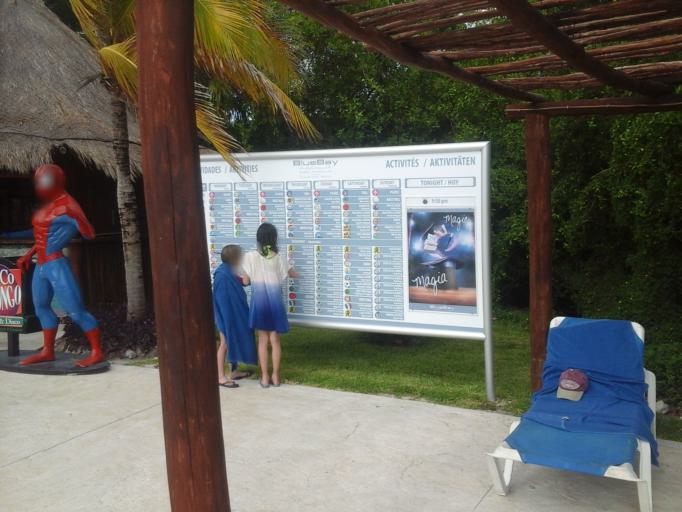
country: MX
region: Quintana Roo
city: Playa del Carmen
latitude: 20.7005
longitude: -87.0126
